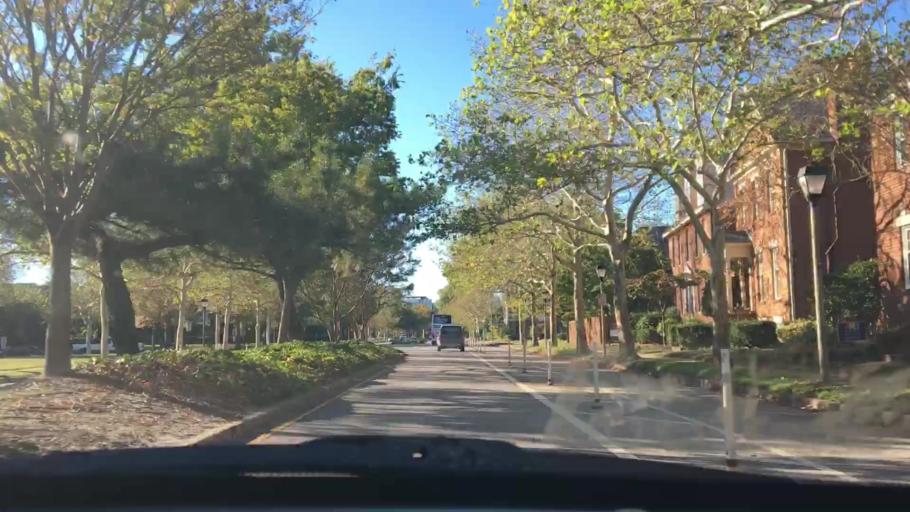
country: US
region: Virginia
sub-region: City of Norfolk
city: Norfolk
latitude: 36.8578
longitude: -76.2941
